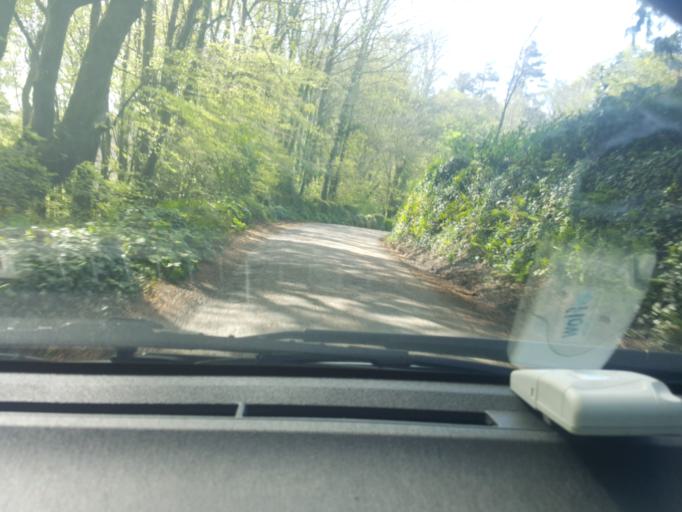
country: IE
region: Munster
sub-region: County Cork
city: Bandon
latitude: 51.7700
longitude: -8.6900
